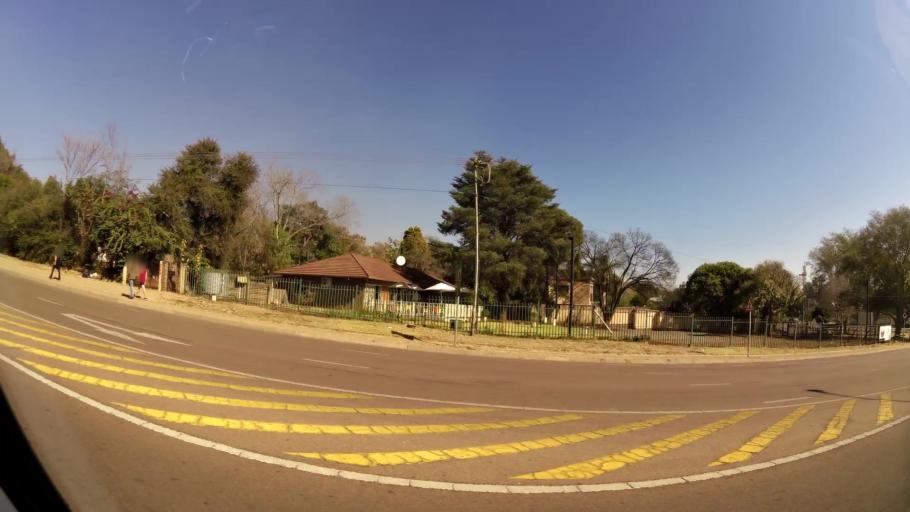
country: ZA
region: Gauteng
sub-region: City of Tshwane Metropolitan Municipality
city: Pretoria
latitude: -25.7746
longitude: 28.2250
